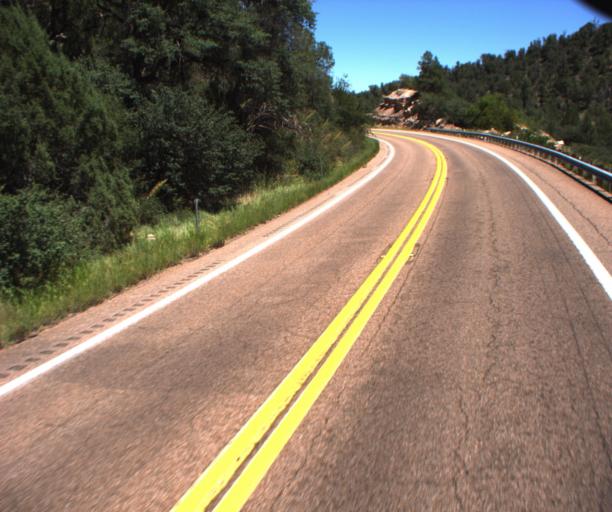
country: US
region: Arizona
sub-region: Navajo County
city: Cibecue
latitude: 33.8428
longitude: -110.4261
